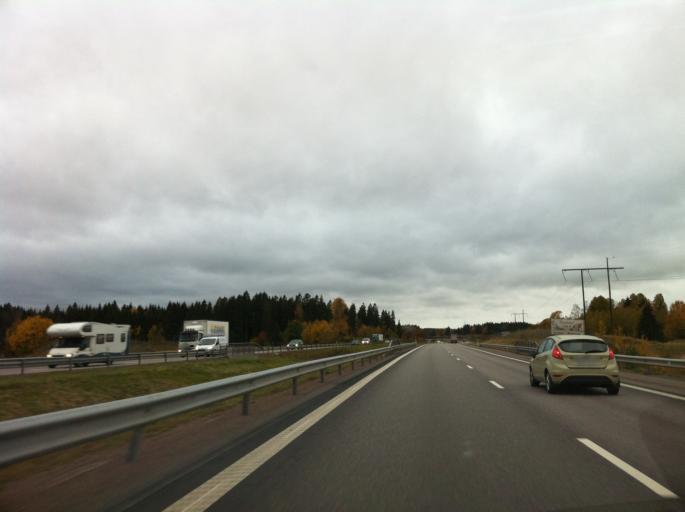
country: SE
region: OEstergoetland
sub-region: Boxholms Kommun
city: Boxholm
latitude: 58.3029
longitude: 14.9625
